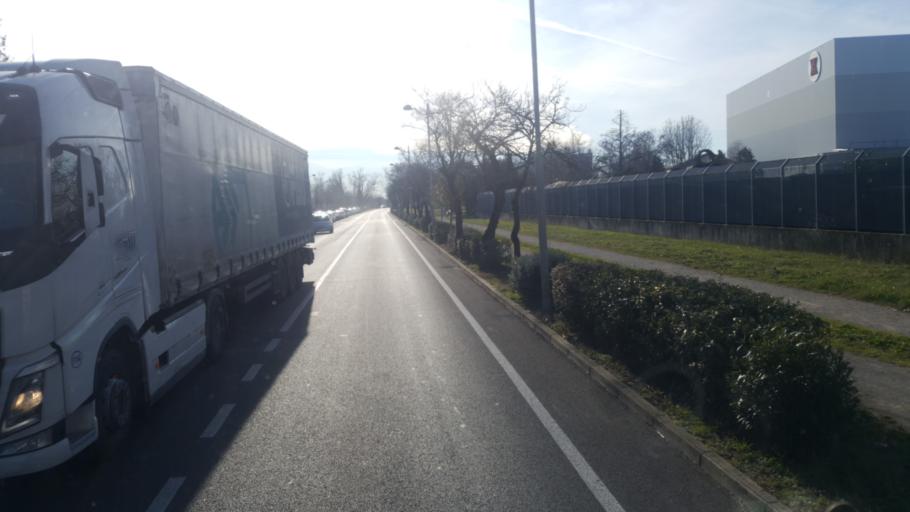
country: IT
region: Friuli Venezia Giulia
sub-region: Provincia di Gorizia
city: Monfalcone
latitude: 45.7945
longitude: 13.5333
